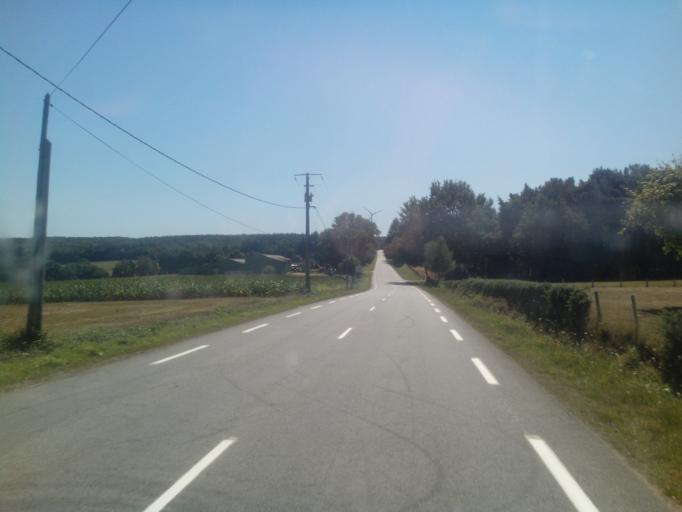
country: FR
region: Brittany
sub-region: Departement du Morbihan
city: Guegon
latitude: 47.9163
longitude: -2.5244
